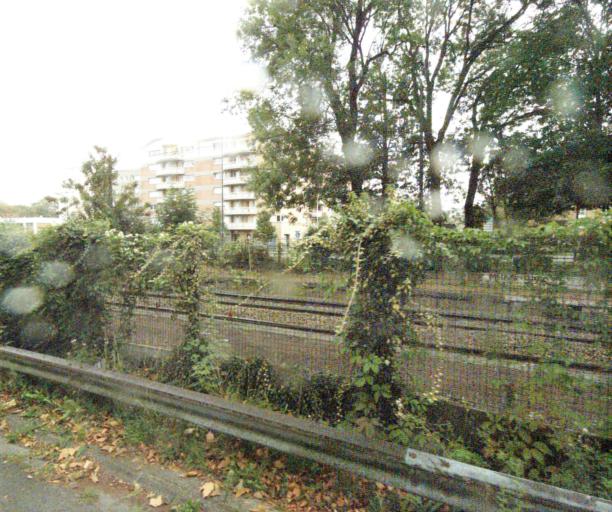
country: FR
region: Nord-Pas-de-Calais
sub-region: Departement du Nord
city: Mons-en-Baroeul
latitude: 50.6240
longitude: 3.1316
